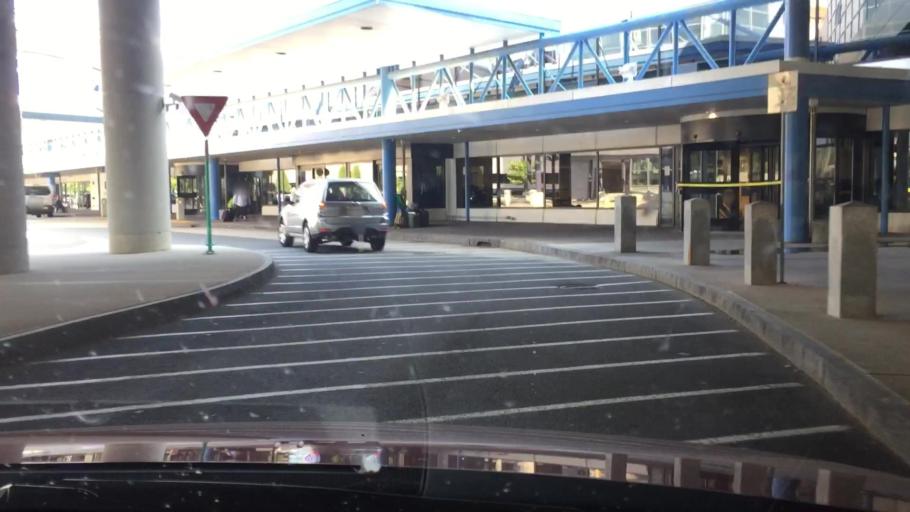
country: US
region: Maine
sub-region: Cumberland County
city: South Portland Gardens
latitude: 43.6477
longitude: -70.3114
